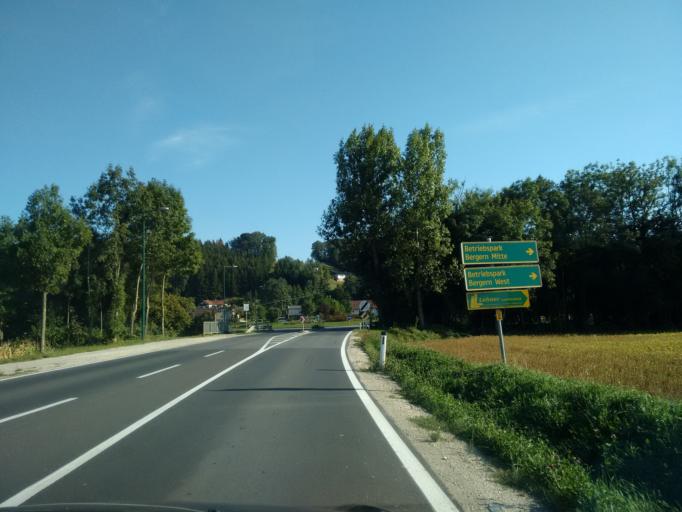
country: AT
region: Upper Austria
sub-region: Wels-Land
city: Marchtrenk
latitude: 48.1671
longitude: 14.1286
